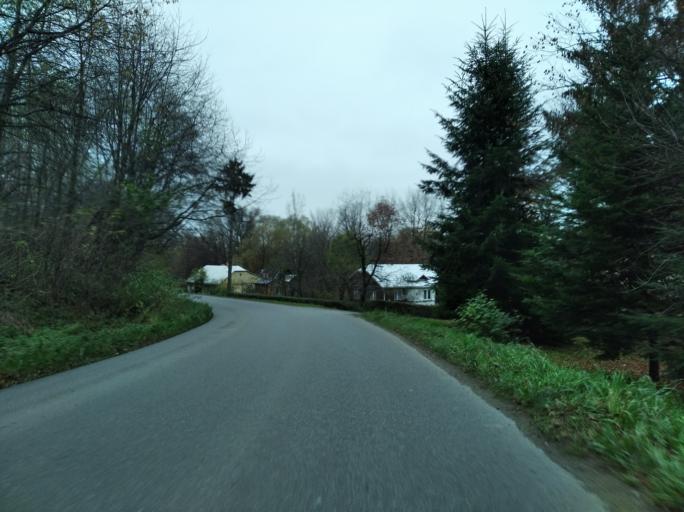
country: PL
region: Subcarpathian Voivodeship
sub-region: Powiat krosnienski
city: Chorkowka
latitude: 49.6751
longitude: 21.6819
